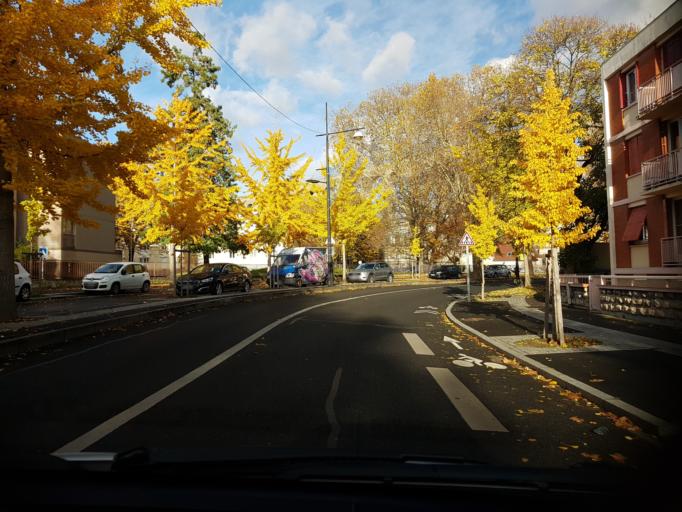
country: FR
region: Ile-de-France
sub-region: Departement du Val-de-Marne
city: Arcueil
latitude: 48.7981
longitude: 2.3329
